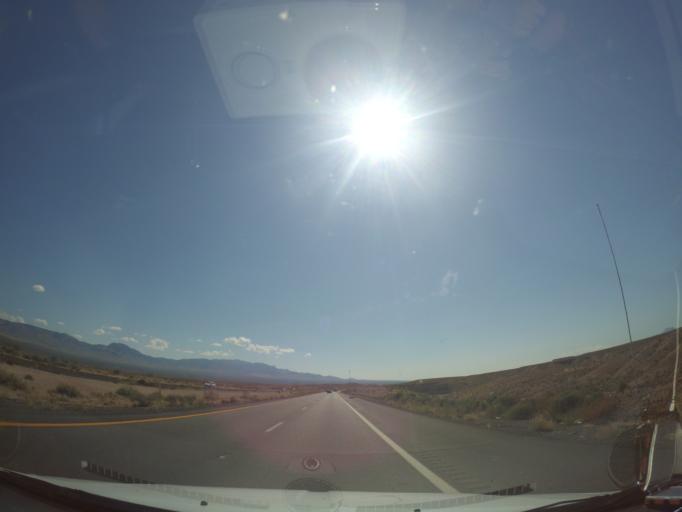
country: US
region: Nevada
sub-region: Clark County
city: Mesquite
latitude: 36.8363
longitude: -114.0019
